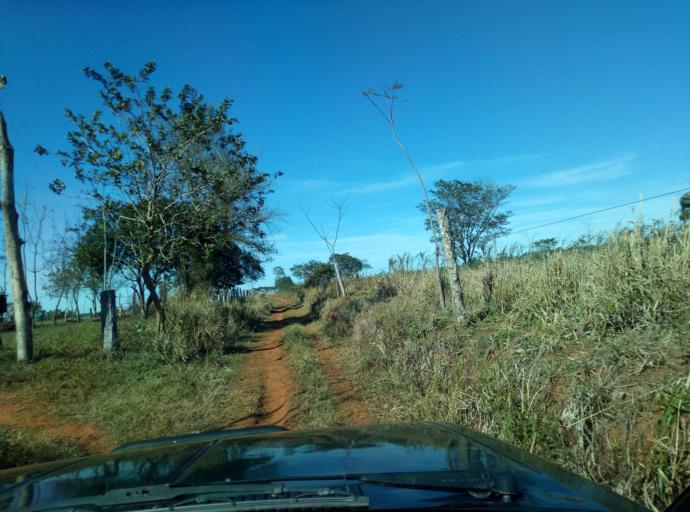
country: PY
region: Caaguazu
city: Doctor Cecilio Baez
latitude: -25.1839
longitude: -56.2423
